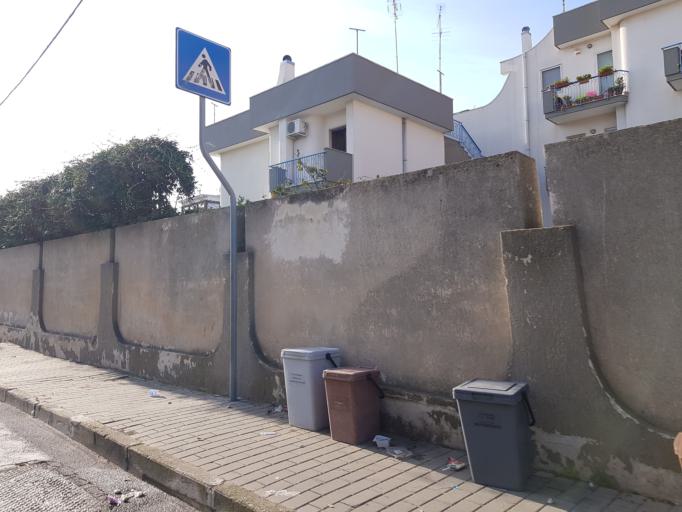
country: IT
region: Apulia
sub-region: Provincia di Brindisi
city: Materdomini
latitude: 40.6548
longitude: 17.9555
